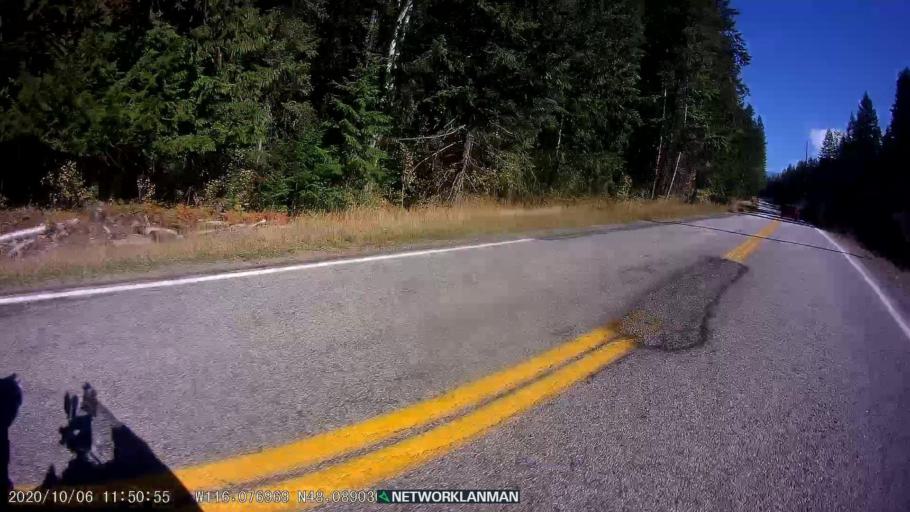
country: US
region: Idaho
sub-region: Bonner County
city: Ponderay
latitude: 48.0890
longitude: -116.0760
